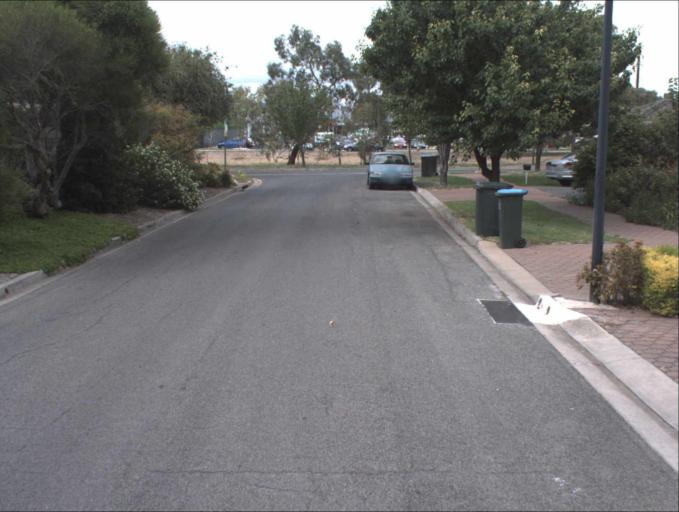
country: AU
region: South Australia
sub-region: Port Adelaide Enfield
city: Gilles Plains
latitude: -34.8538
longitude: 138.6544
